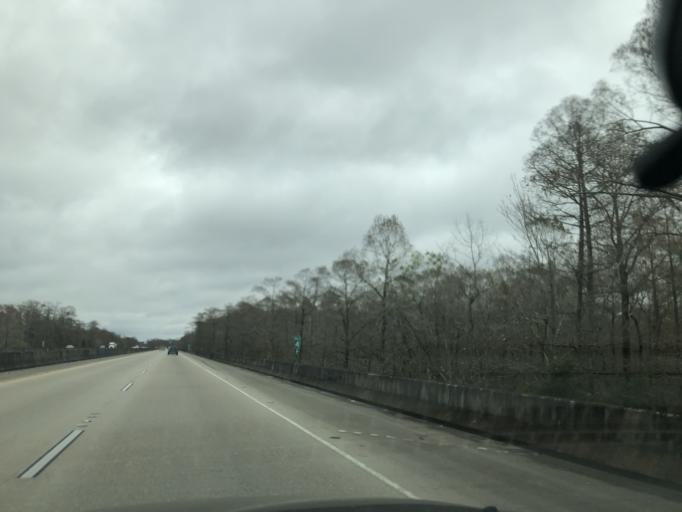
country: US
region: Louisiana
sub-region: Saint Charles Parish
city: Destrehan
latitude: 29.9647
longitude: -90.3473
